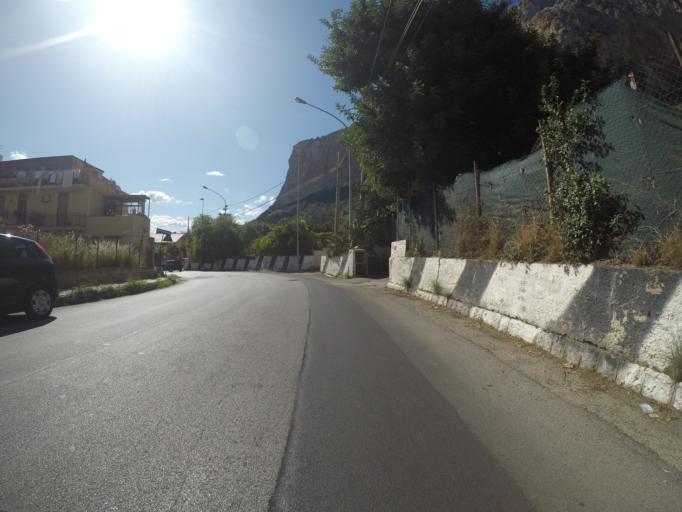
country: IT
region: Sicily
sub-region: Palermo
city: Palermo
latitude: 38.1658
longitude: 13.3658
